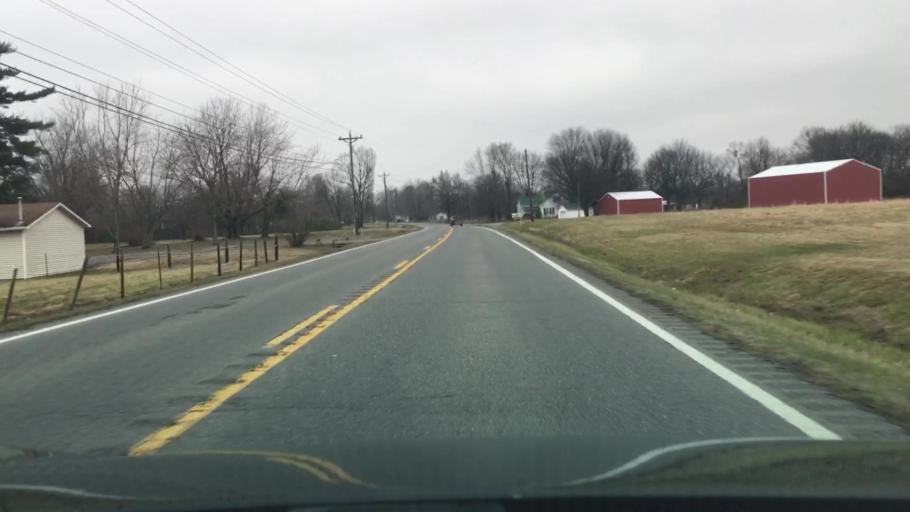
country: US
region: Kentucky
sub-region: Marshall County
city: Calvert City
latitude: 36.9676
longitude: -88.3850
